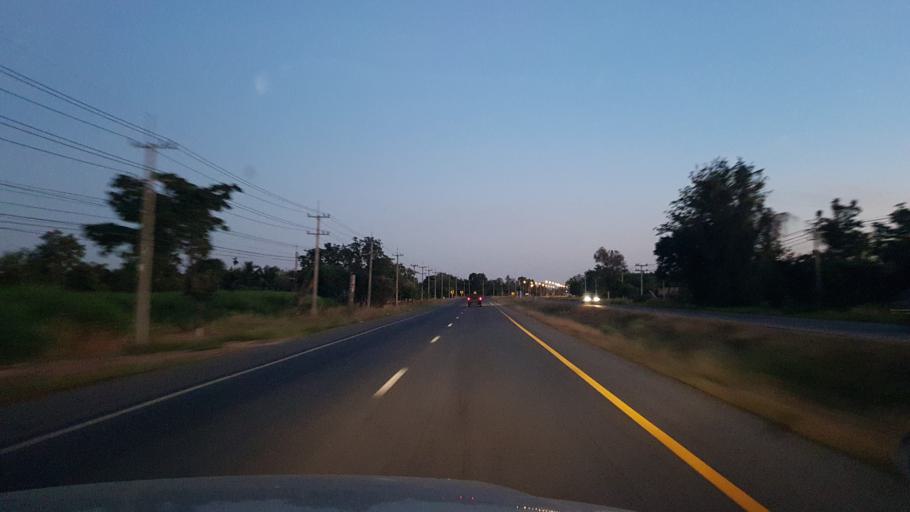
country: TH
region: Chaiyaphum
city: Phu Khiao
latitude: 16.3058
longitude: 102.2056
